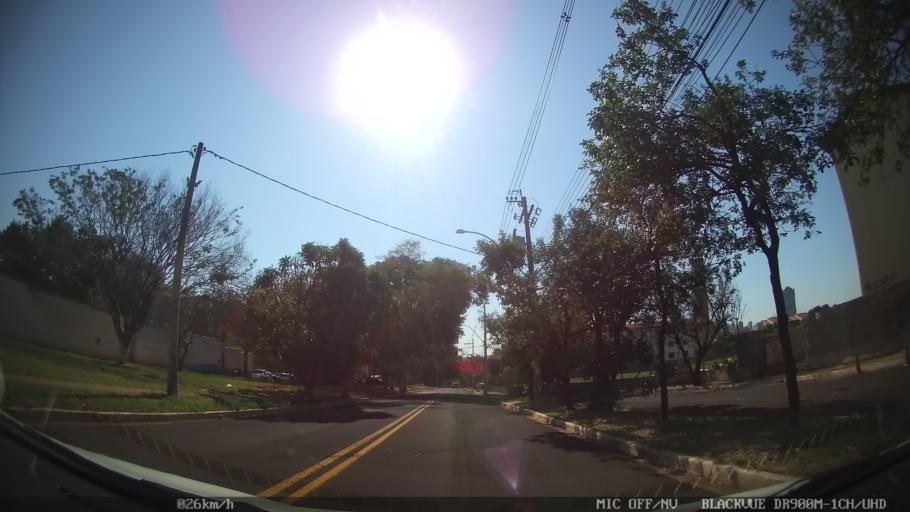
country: BR
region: Sao Paulo
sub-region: Ribeirao Preto
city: Ribeirao Preto
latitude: -21.2125
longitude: -47.8272
